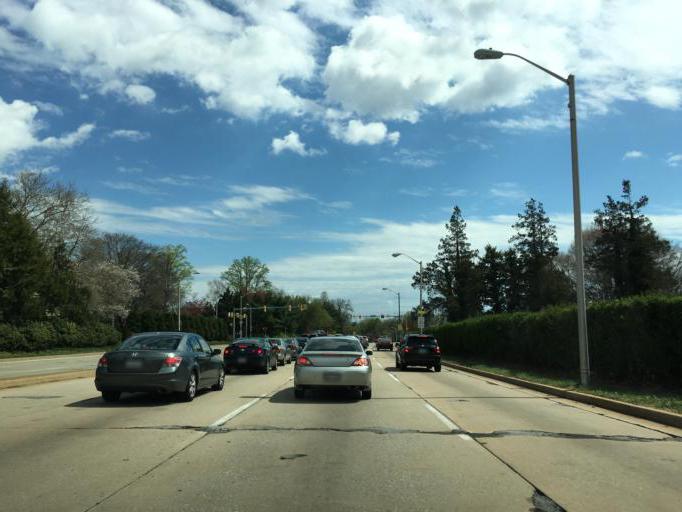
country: US
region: Maryland
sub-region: Baltimore County
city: Towson
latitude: 39.3622
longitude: -76.6362
